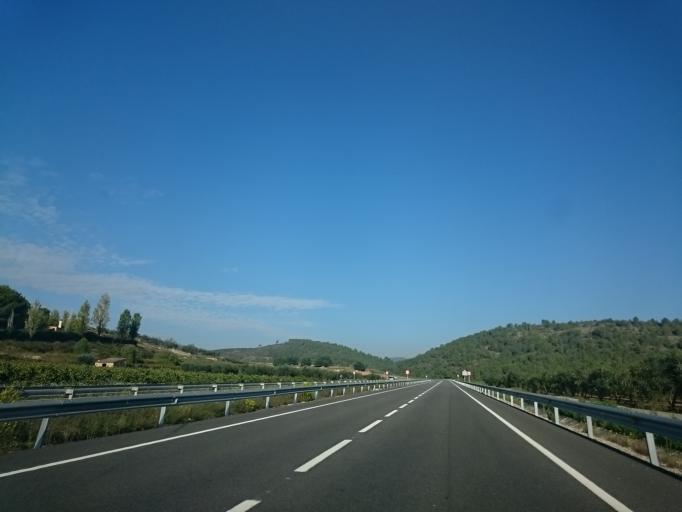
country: ES
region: Catalonia
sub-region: Provincia de Tarragona
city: Albinyana
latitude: 41.2664
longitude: 1.4862
